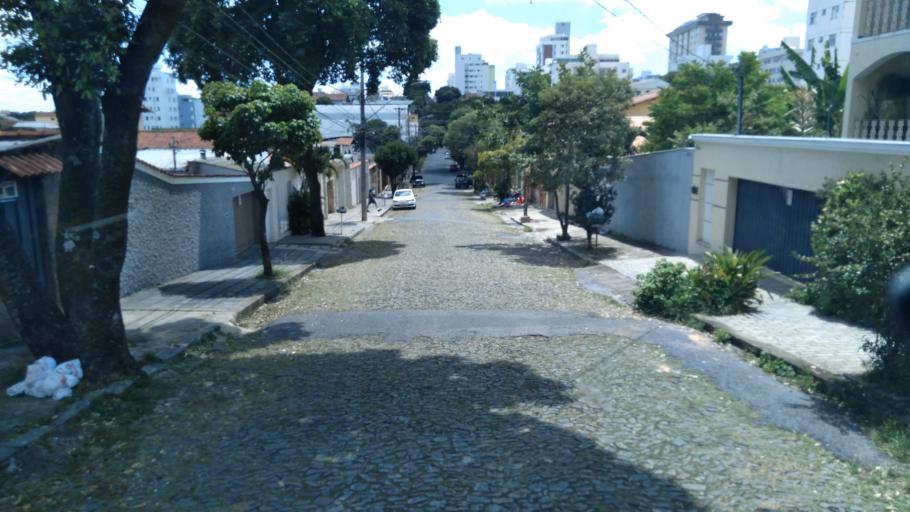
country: BR
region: Minas Gerais
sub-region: Belo Horizonte
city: Belo Horizonte
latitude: -19.8898
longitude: -43.9072
